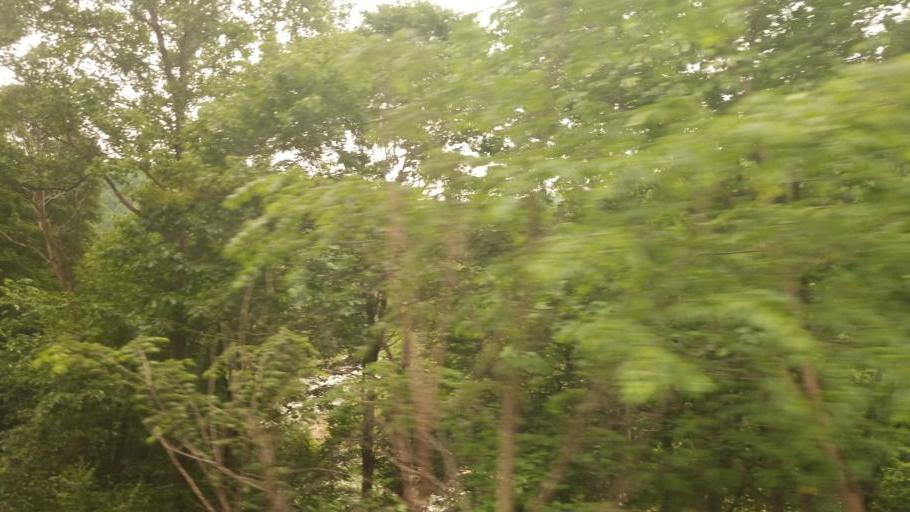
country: US
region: Pennsylvania
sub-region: Fayette County
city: South Connellsville
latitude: 39.9048
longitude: -79.4772
